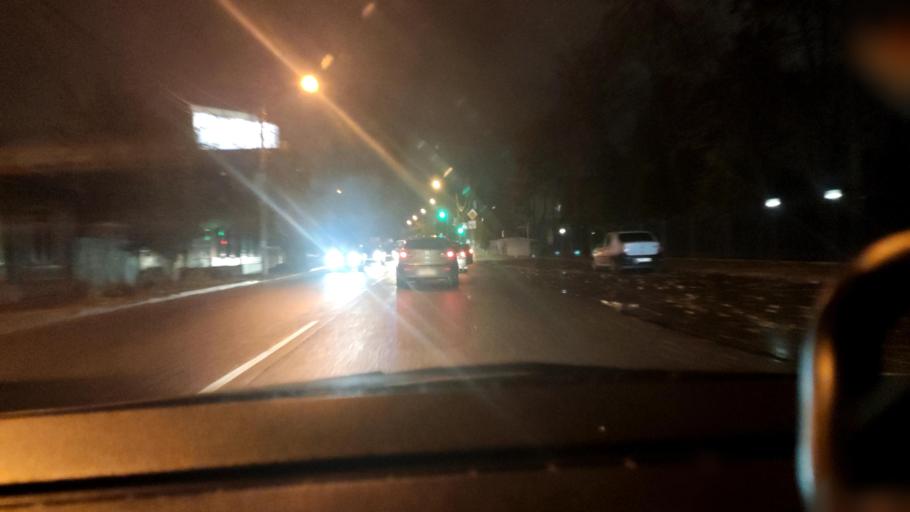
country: RU
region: Voronezj
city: Voronezh
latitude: 51.6843
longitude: 39.2124
